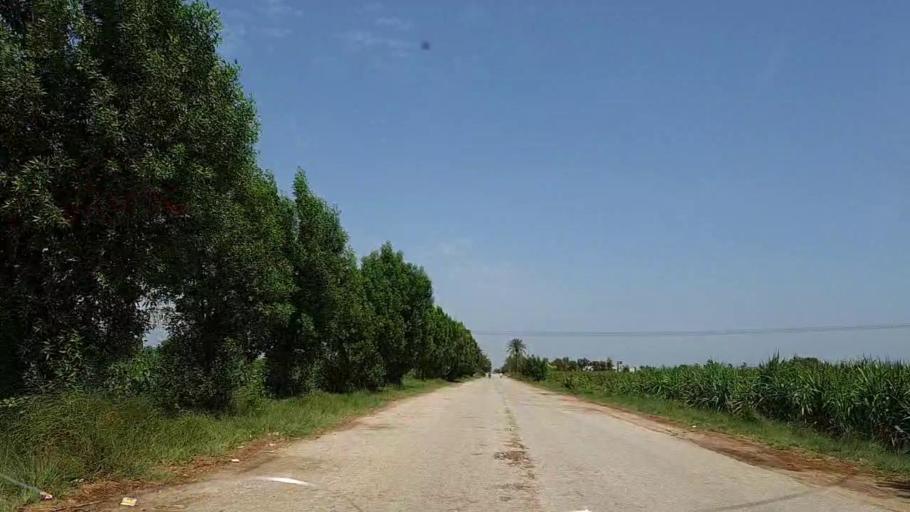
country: PK
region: Sindh
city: Naushahro Firoz
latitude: 26.8319
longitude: 68.1362
